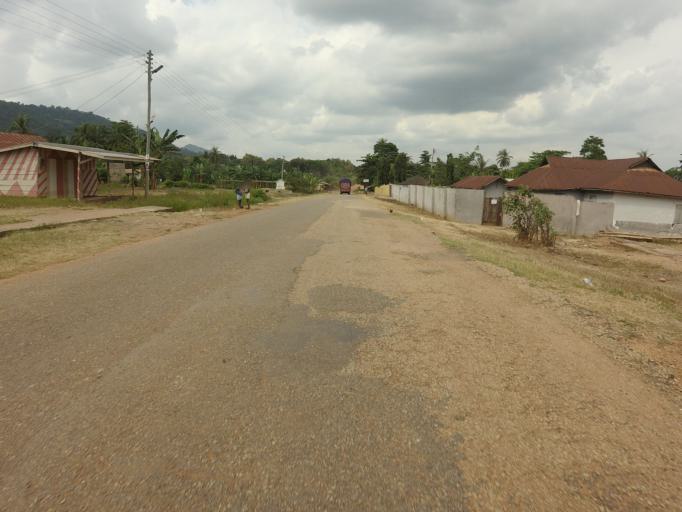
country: GH
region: Volta
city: Ho
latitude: 6.6515
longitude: 0.3416
